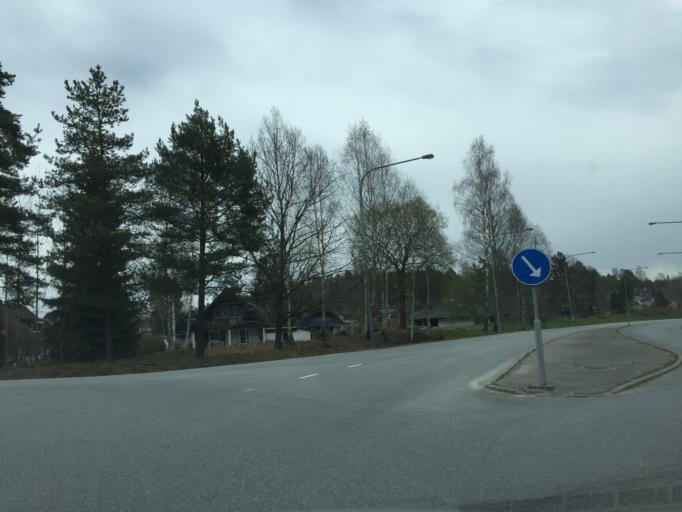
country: SE
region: OErebro
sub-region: Orebro Kommun
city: Orebro
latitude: 59.2433
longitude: 15.2444
